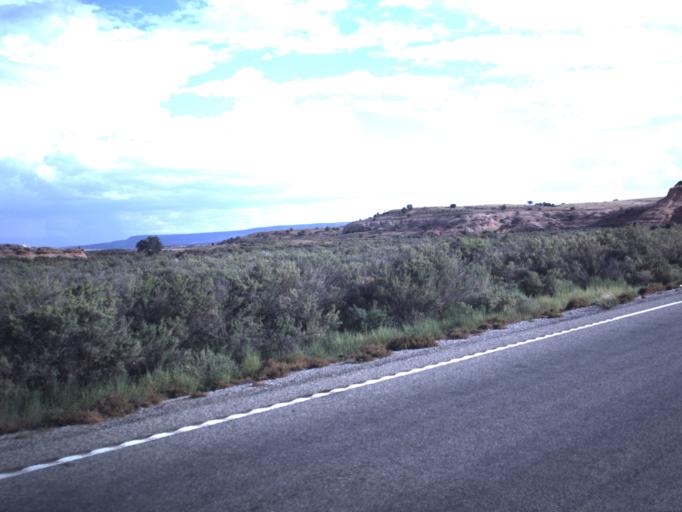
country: US
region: Utah
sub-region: San Juan County
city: Monticello
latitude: 38.1979
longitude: -109.3757
